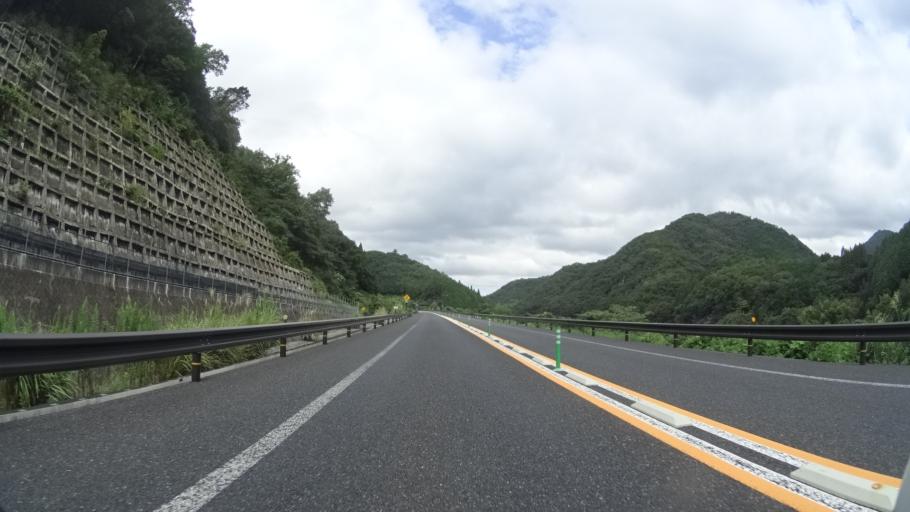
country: JP
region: Hyogo
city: Yamazakicho-nakabirose
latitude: 35.0599
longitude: 134.3646
